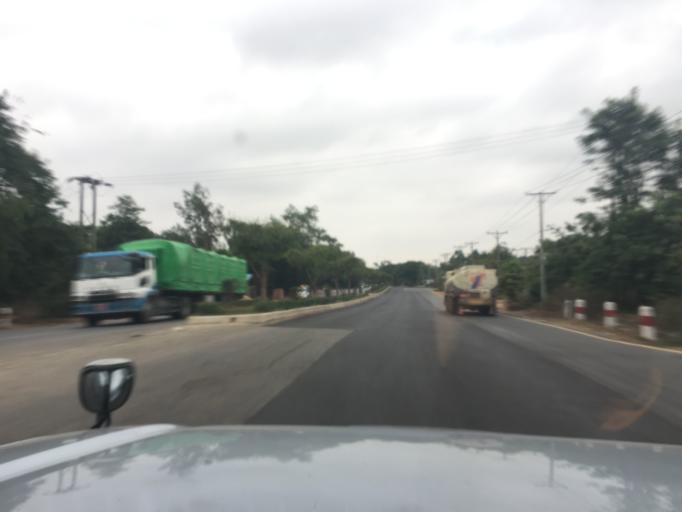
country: MM
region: Bago
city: Bago
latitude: 17.2317
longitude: 96.4589
